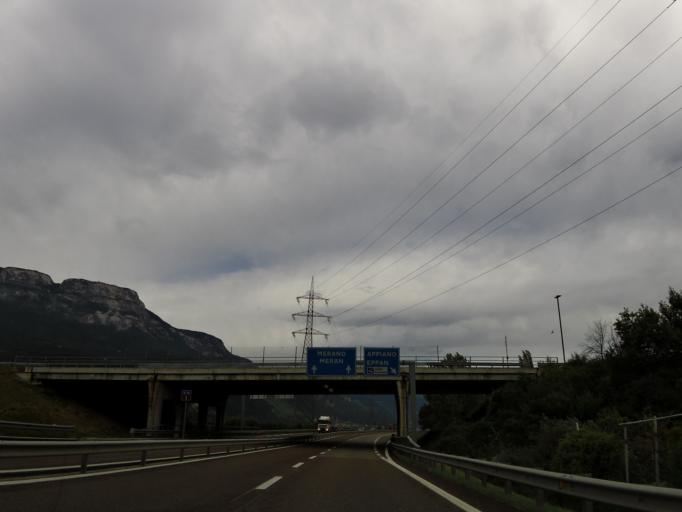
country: IT
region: Trentino-Alto Adige
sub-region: Bolzano
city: Cornaiano
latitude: 46.4857
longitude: 11.2907
